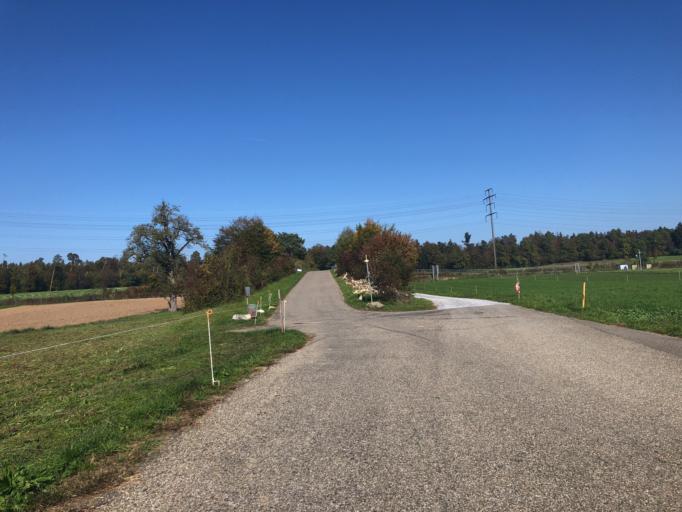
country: CH
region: Zurich
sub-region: Bezirk Uster
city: Naenikon / Naenikon (Dorfkern)
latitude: 47.3732
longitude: 8.6963
